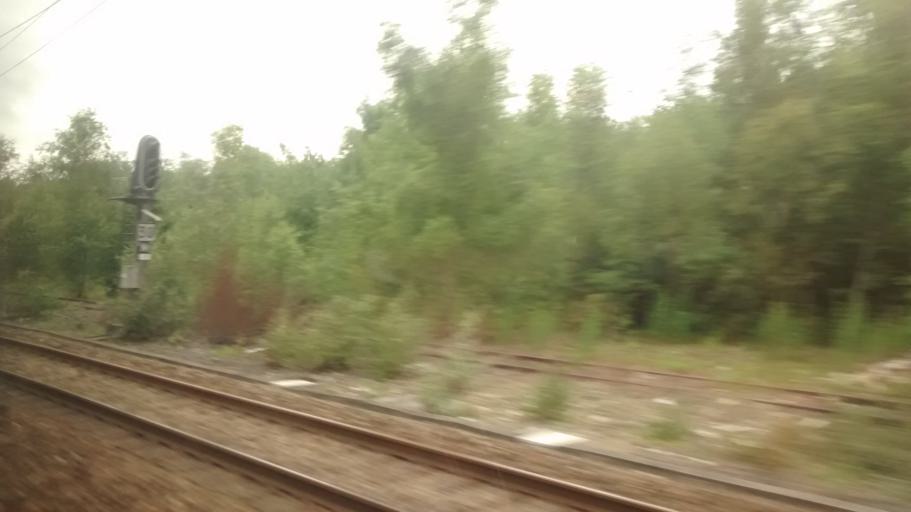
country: FR
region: Pays de la Loire
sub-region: Departement de la Mayenne
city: Argentre
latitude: 48.1298
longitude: -0.6430
